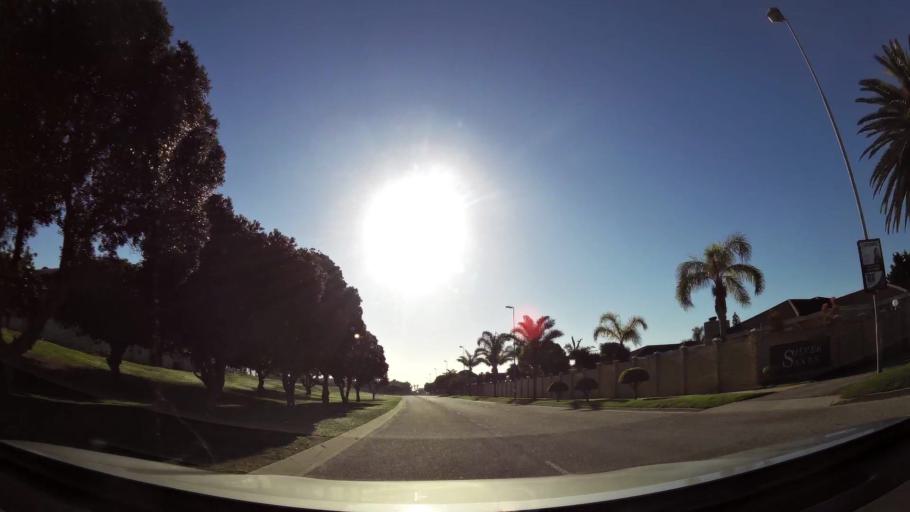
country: ZA
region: Eastern Cape
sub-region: Nelson Mandela Bay Metropolitan Municipality
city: Port Elizabeth
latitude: -33.9896
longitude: 25.6529
